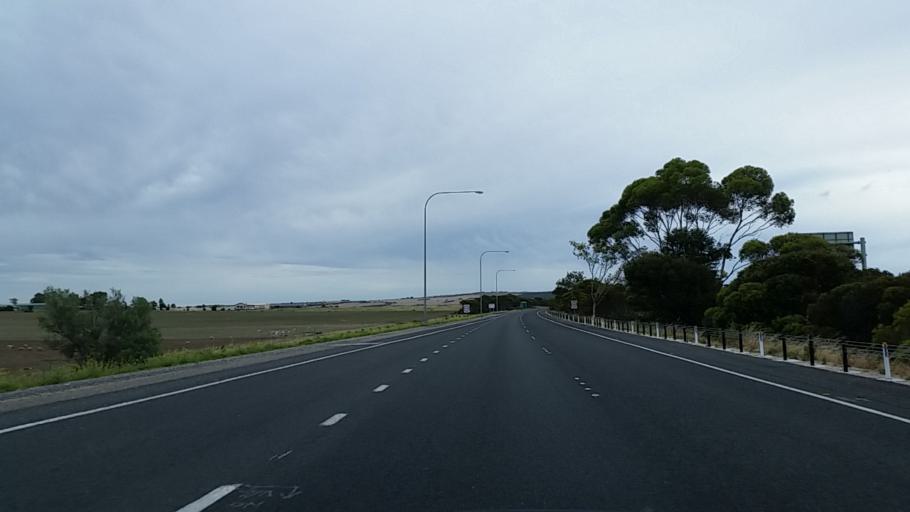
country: AU
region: South Australia
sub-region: Murray Bridge
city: Murray Bridge
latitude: -35.1514
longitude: 139.2818
